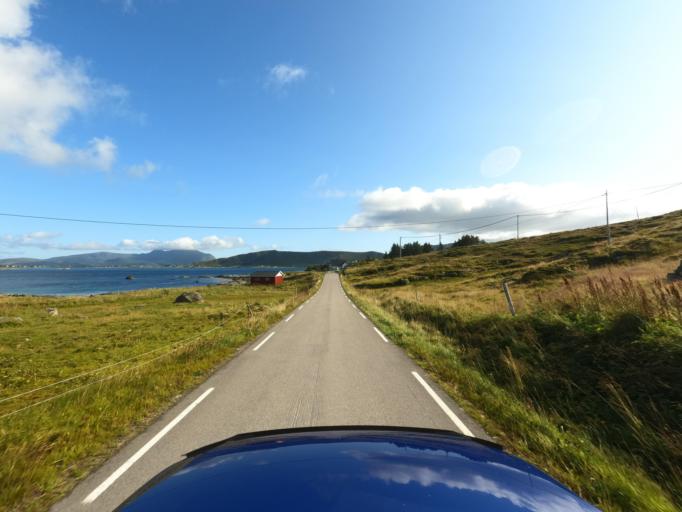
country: NO
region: Nordland
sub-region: Vestvagoy
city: Gravdal
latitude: 68.1453
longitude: 13.4505
